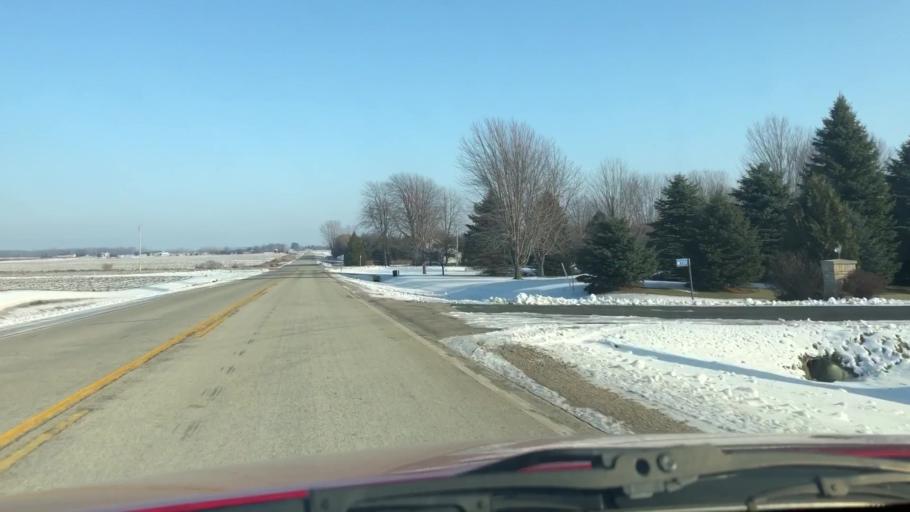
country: US
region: Wisconsin
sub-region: Outagamie County
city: Seymour
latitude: 44.4436
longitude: -88.3528
